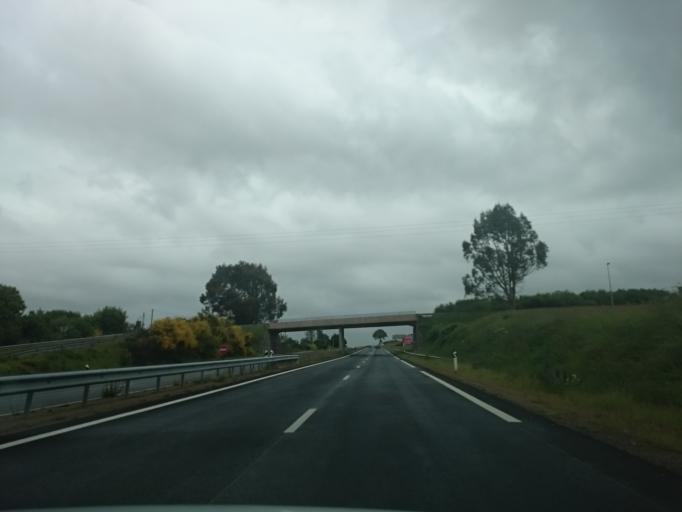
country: FR
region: Brittany
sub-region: Departement des Cotes-d'Armor
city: Cavan
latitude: 48.6921
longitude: -3.3695
